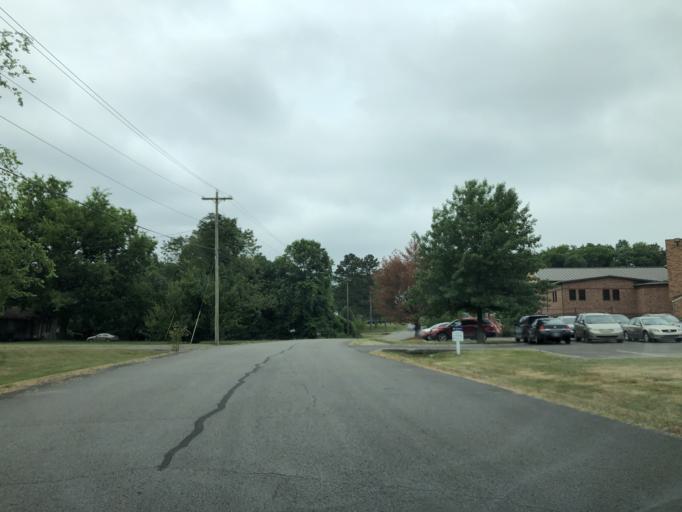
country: US
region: Tennessee
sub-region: Davidson County
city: Goodlettsville
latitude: 36.2842
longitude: -86.7316
